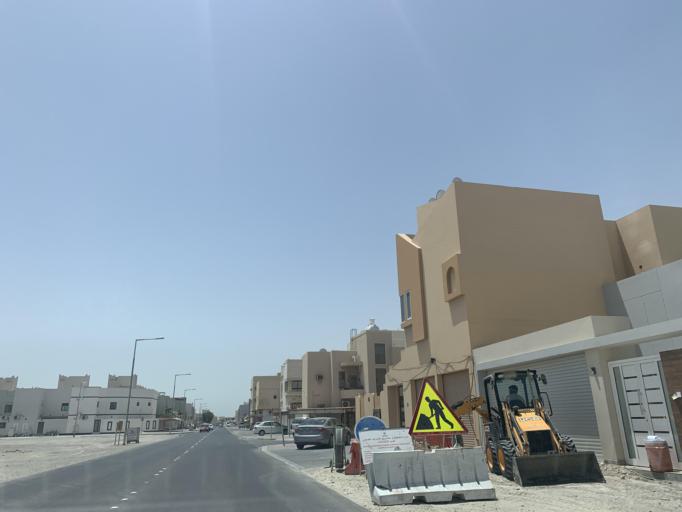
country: BH
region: Northern
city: Sitrah
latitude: 26.1618
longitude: 50.6225
